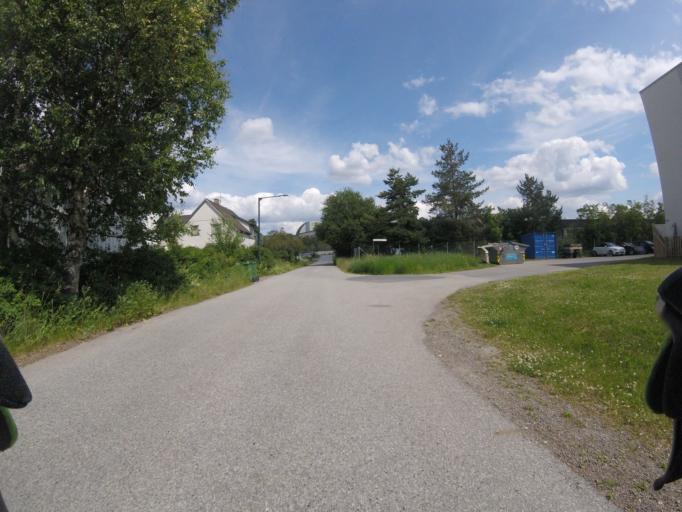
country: NO
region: Akershus
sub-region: Skedsmo
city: Lillestrom
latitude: 59.9713
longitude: 11.0478
